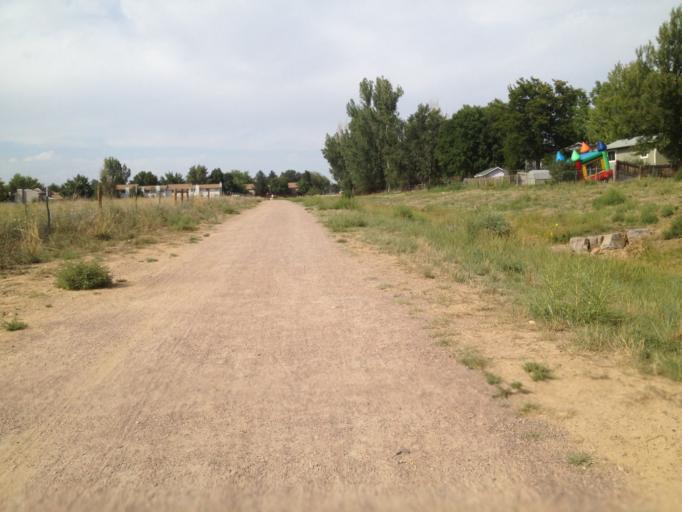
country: US
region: Colorado
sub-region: Boulder County
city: Louisville
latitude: 39.9809
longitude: -105.1142
